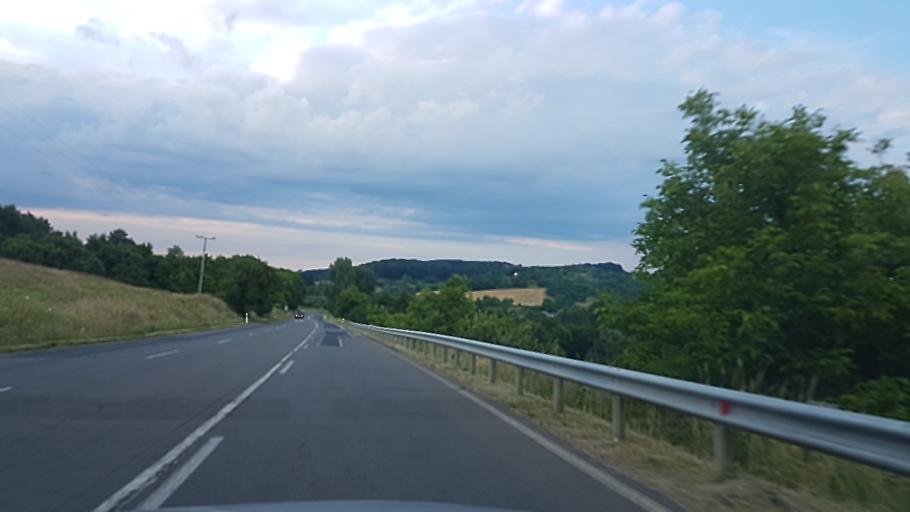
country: HU
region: Somogy
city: Kaposvar
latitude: 46.2782
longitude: 17.8214
